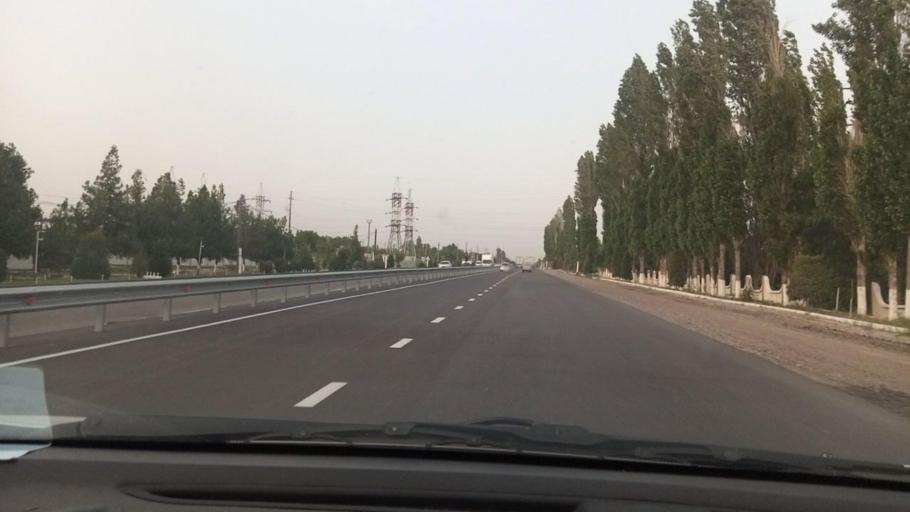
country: UZ
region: Toshkent
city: Angren
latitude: 40.9766
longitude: 70.0055
